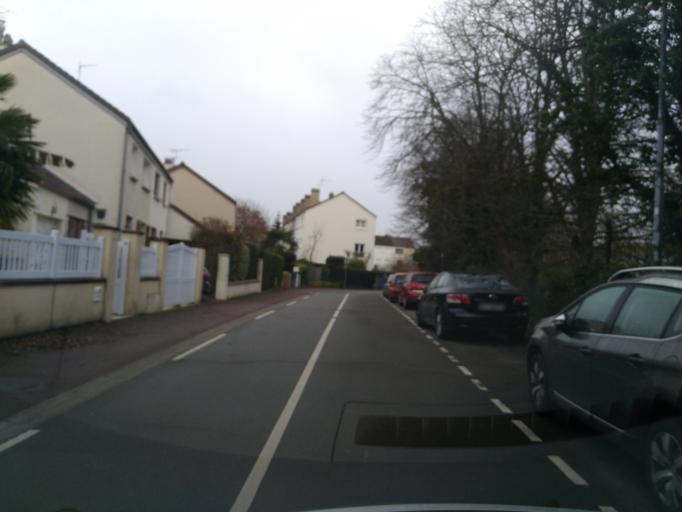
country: FR
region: Ile-de-France
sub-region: Departement des Yvelines
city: Villepreux
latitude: 48.8286
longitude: 2.0047
